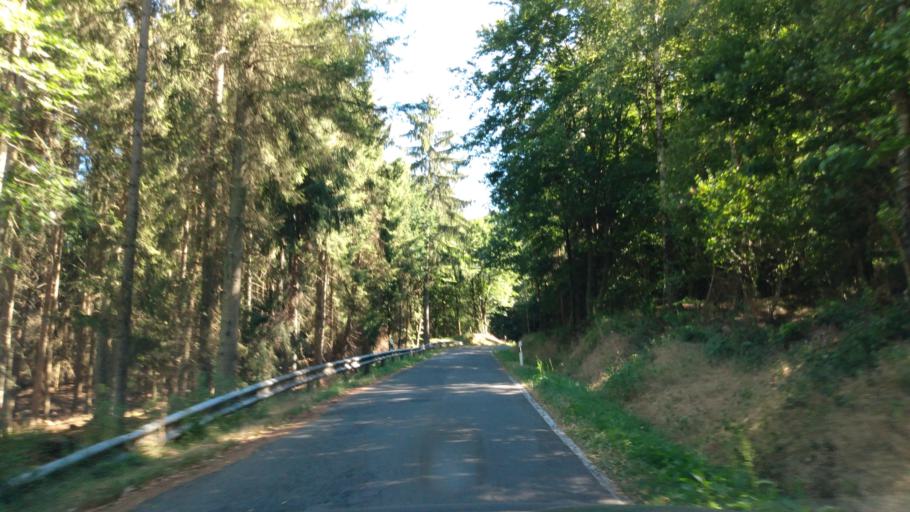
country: DE
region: Rheinland-Pfalz
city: Landscheid
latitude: 50.0180
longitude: 6.7650
